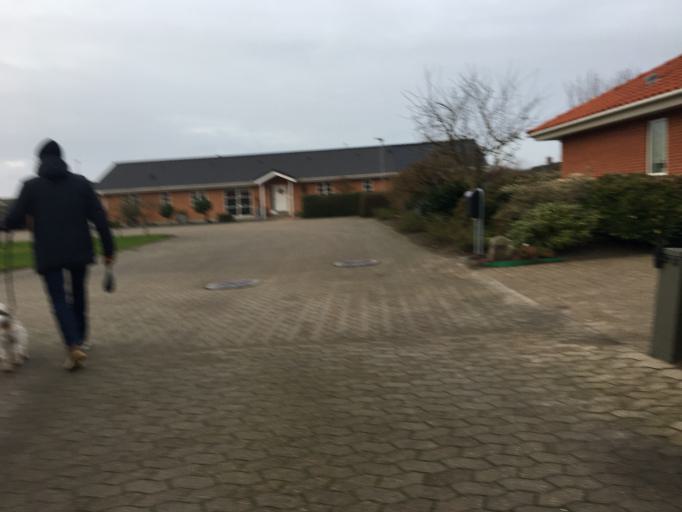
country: DK
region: Central Jutland
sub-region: Ringkobing-Skjern Kommune
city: Ringkobing
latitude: 56.0986
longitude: 8.2638
